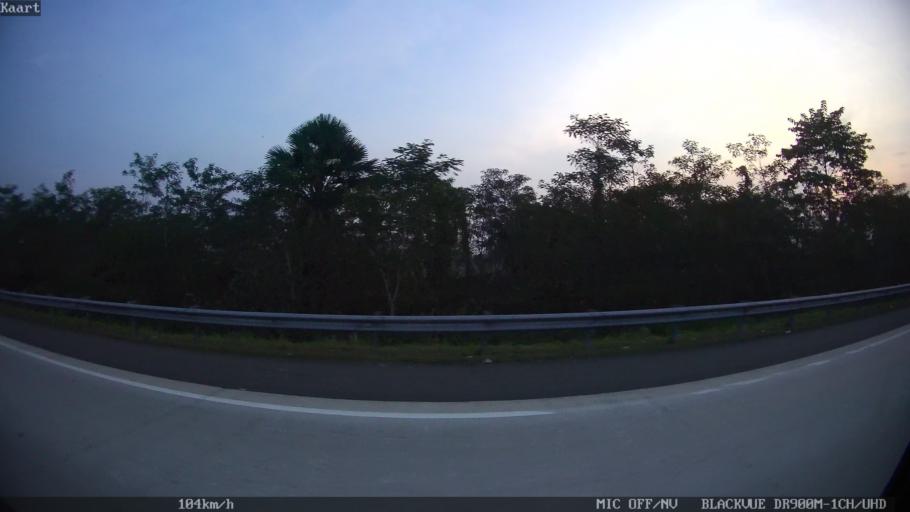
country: ID
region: Lampung
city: Pasuruan
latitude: -5.7068
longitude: 105.6415
